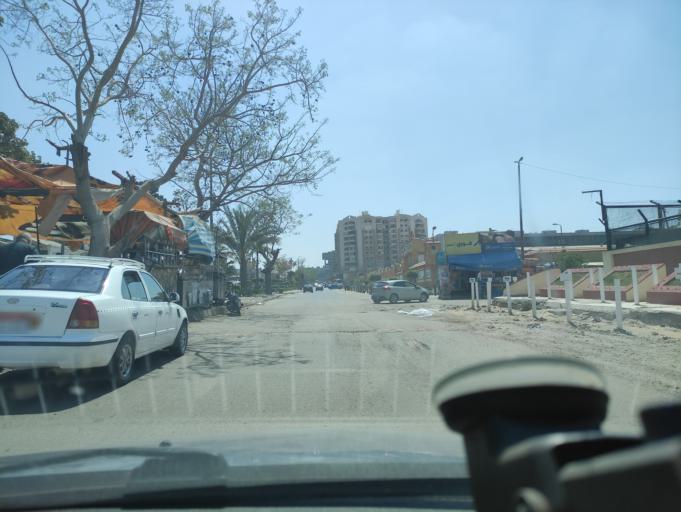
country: EG
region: Muhafazat al Qahirah
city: Cairo
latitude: 30.0410
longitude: 31.3459
